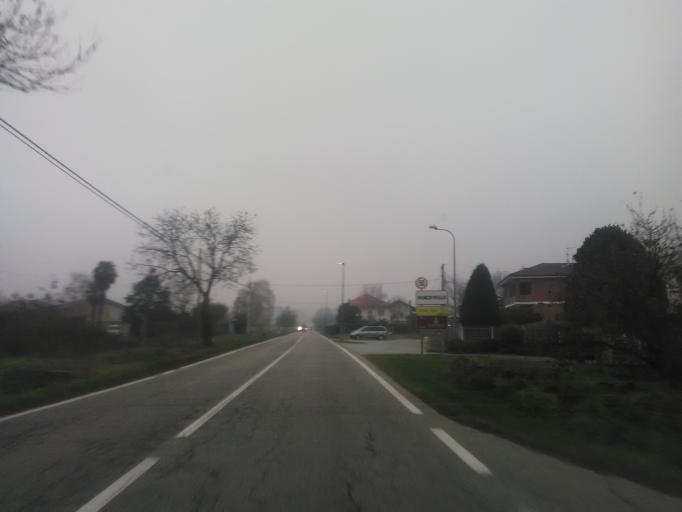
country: IT
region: Piedmont
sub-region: Provincia di Vercelli
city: Moncrivello
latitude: 45.3238
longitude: 8.0110
